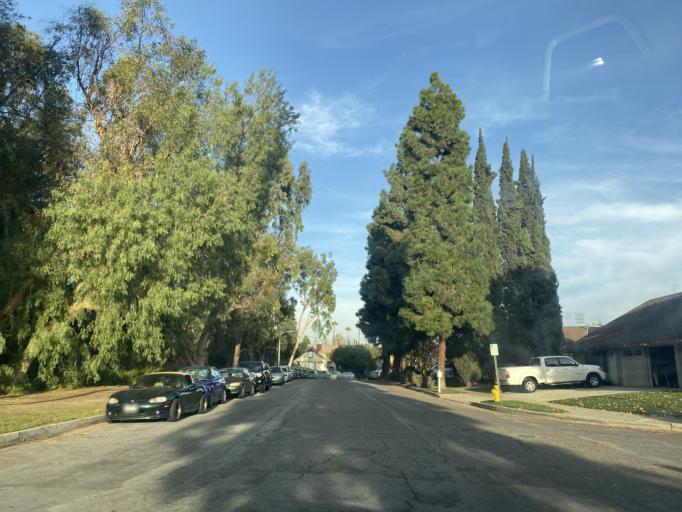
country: US
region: California
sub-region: Orange County
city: Placentia
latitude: 33.8862
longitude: -117.8917
